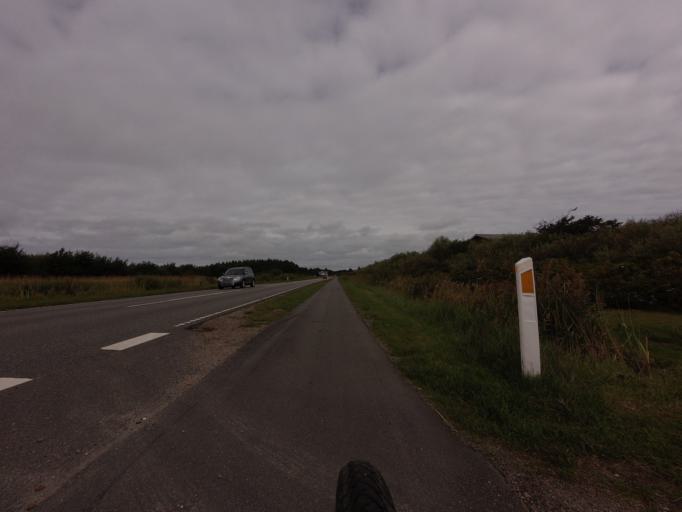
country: DK
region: North Denmark
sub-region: Hjorring Kommune
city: Hirtshals
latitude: 57.5699
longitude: 9.9425
